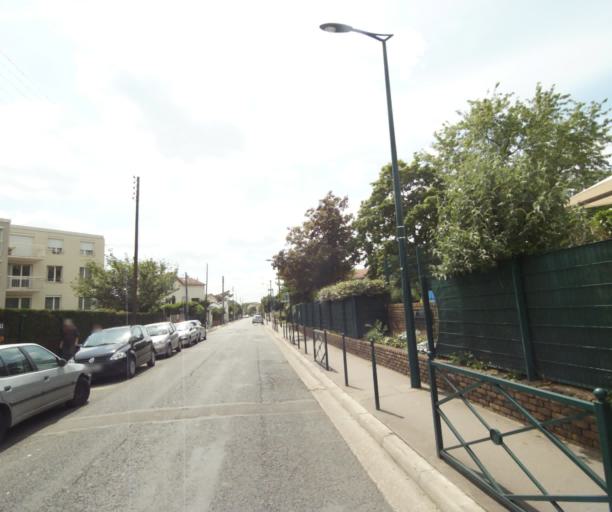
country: FR
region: Ile-de-France
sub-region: Departement des Hauts-de-Seine
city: Colombes
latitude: 48.9204
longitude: 2.2470
